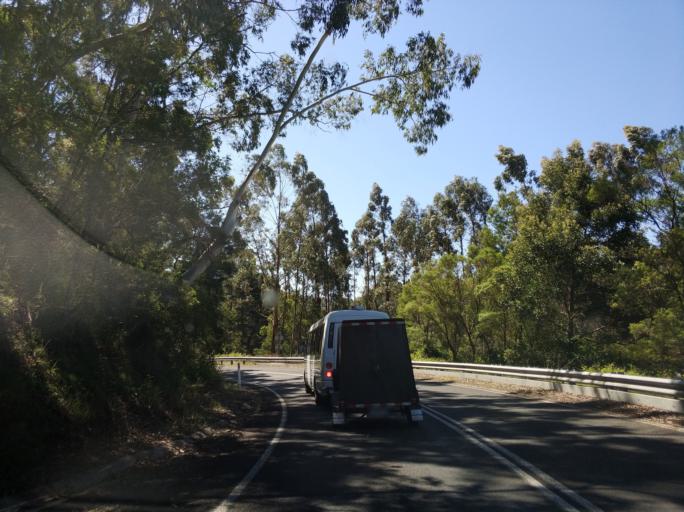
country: AU
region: Victoria
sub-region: Colac-Otway
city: Apollo Bay
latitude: -38.7302
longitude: 143.2534
